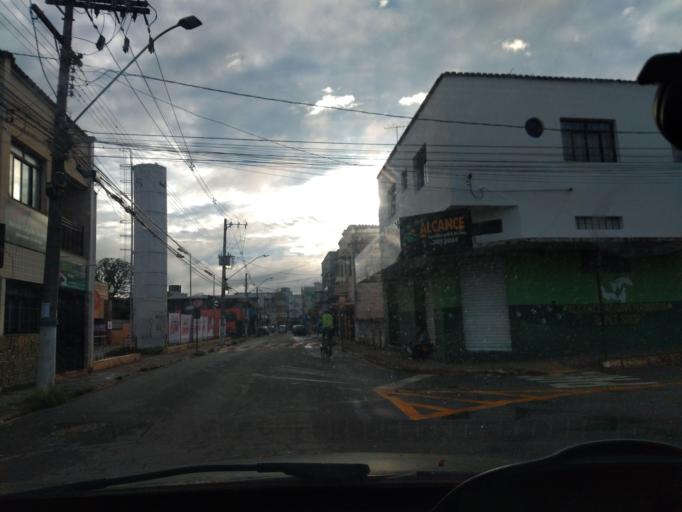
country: BR
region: Minas Gerais
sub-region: Lavras
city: Lavras
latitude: -21.2478
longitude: -45.0077
